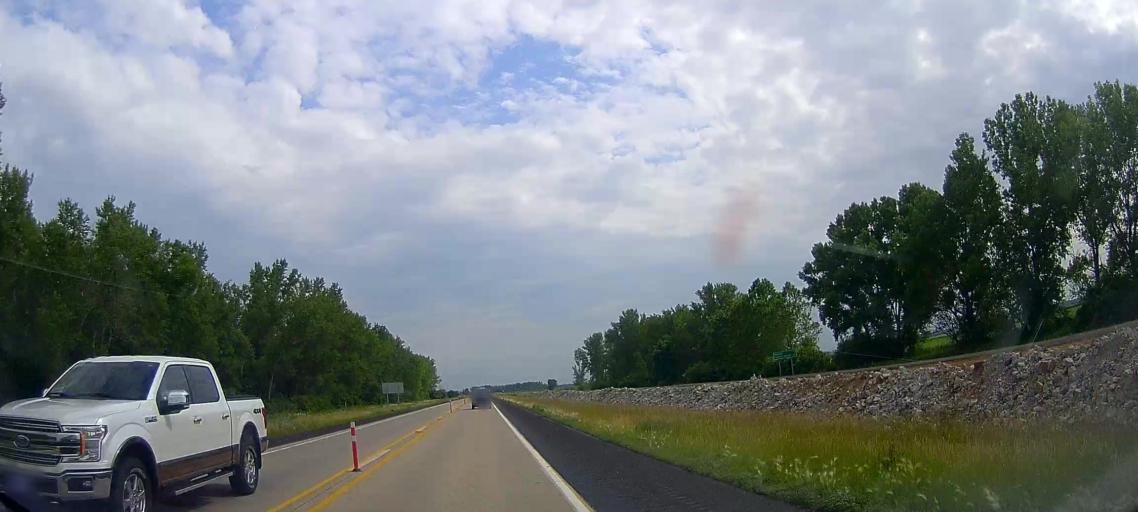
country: US
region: Nebraska
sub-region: Washington County
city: Blair
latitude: 41.6987
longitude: -96.0430
